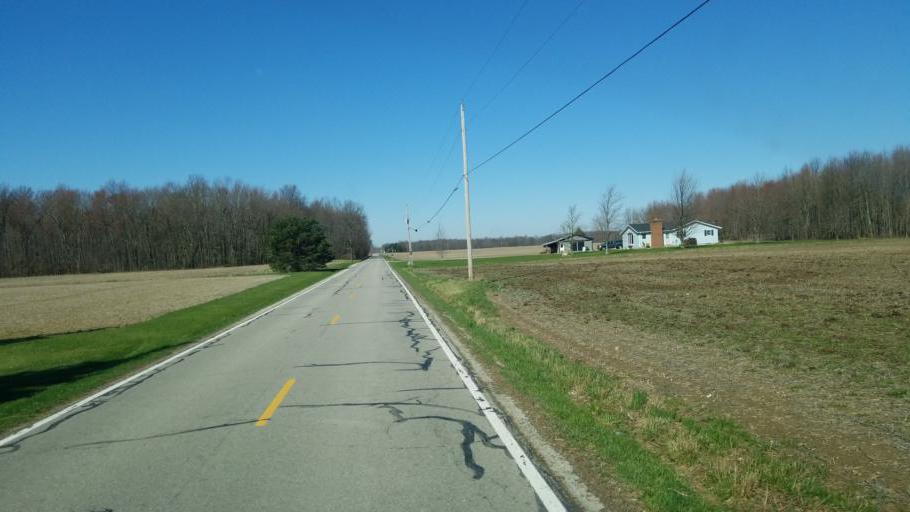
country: US
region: Ohio
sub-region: Huron County
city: Willard
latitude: 40.9820
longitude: -82.8244
